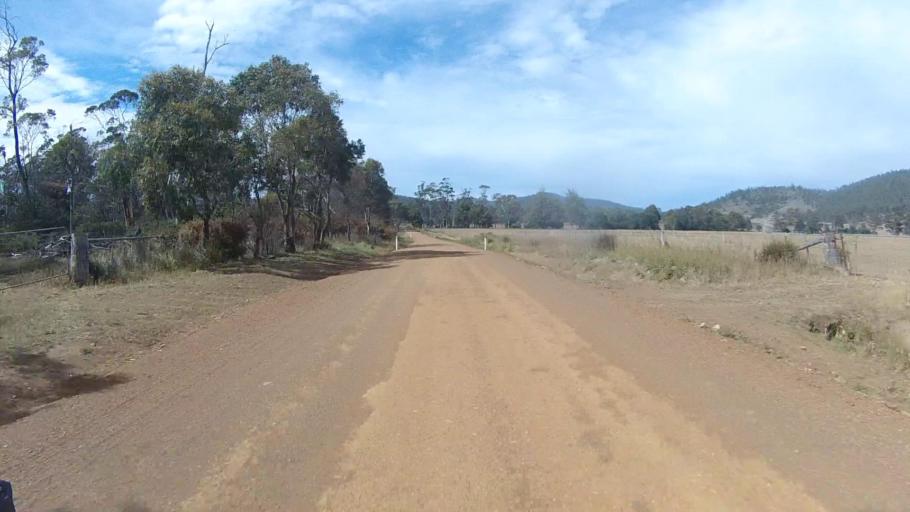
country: AU
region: Tasmania
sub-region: Sorell
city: Sorell
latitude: -42.6382
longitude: 147.9003
